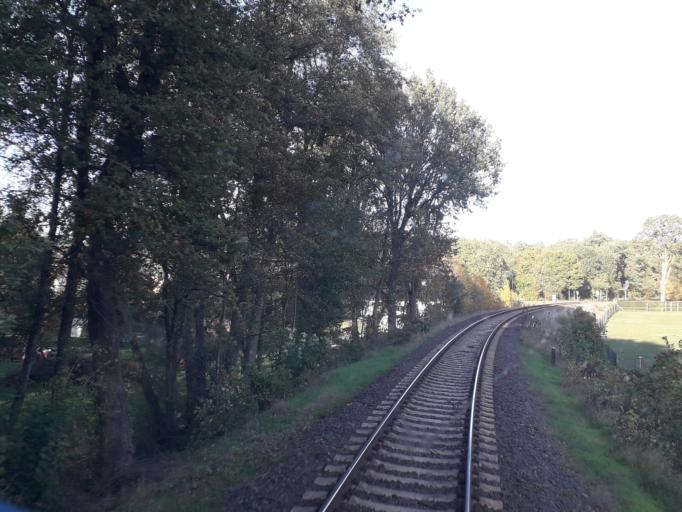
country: DE
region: Brandenburg
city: Wittenberge
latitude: 53.0181
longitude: 11.7618
